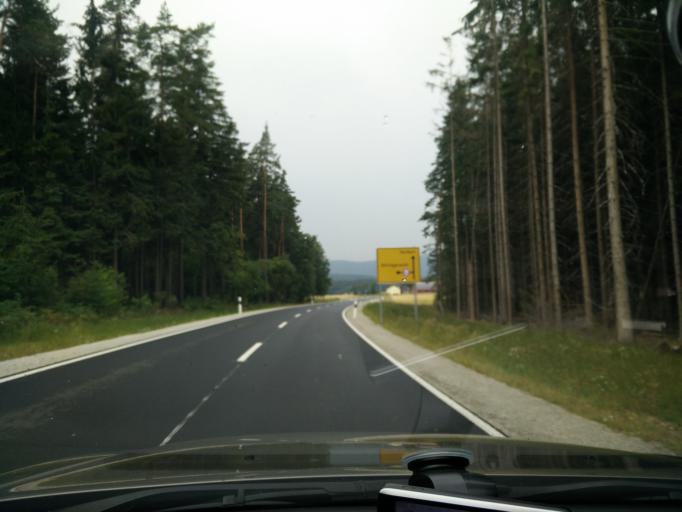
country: DE
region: Bavaria
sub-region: Upper Franconia
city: Trostau
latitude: 50.0430
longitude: 11.9653
